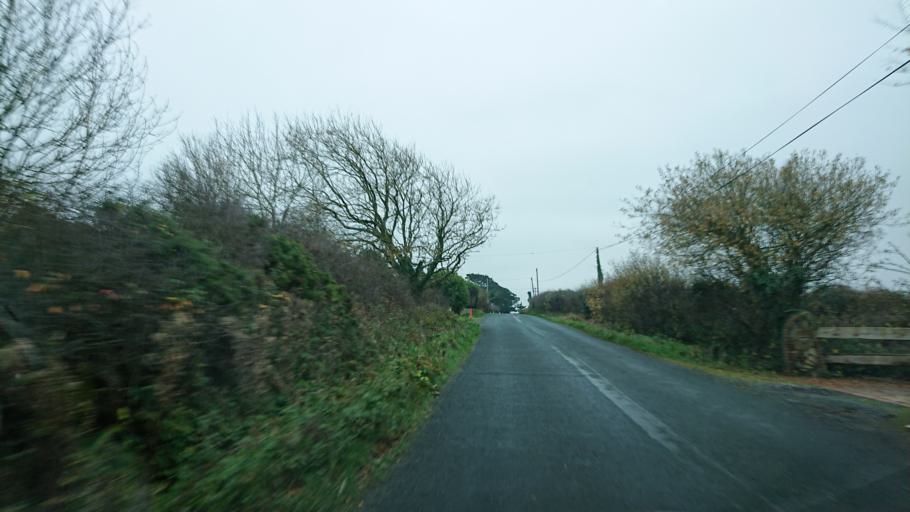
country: IE
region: Munster
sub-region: Waterford
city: Dunmore East
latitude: 52.1664
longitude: -7.0657
